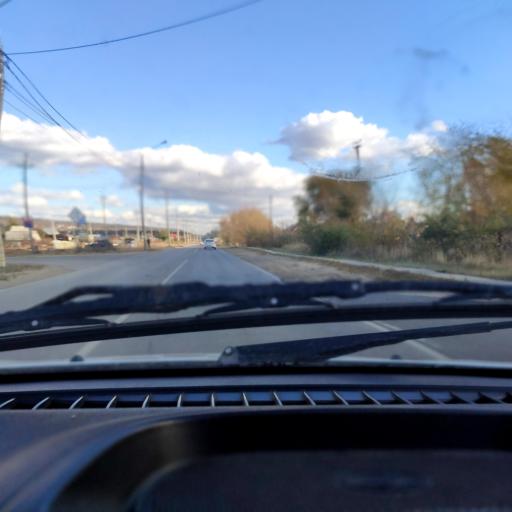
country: RU
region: Samara
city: Zhigulevsk
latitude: 53.4636
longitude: 49.5830
